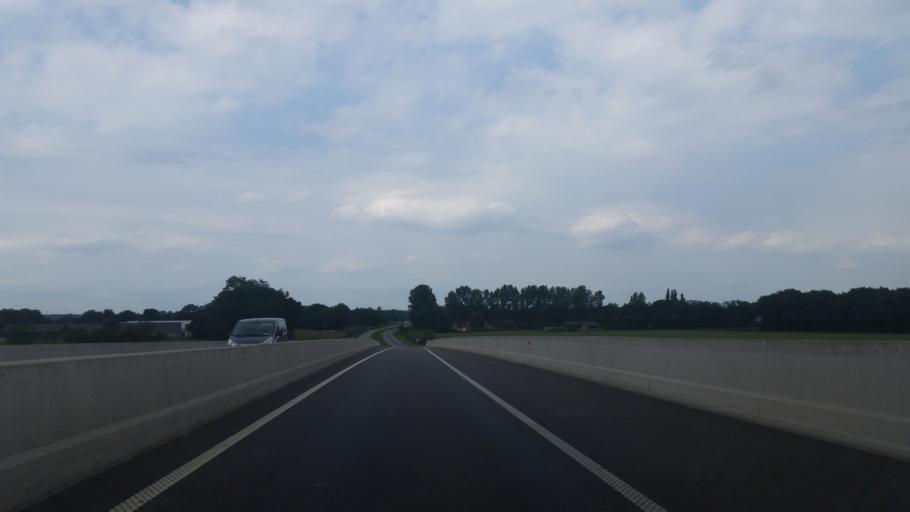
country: BE
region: Flanders
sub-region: Provincie Antwerpen
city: Geel
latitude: 51.1999
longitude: 4.9702
